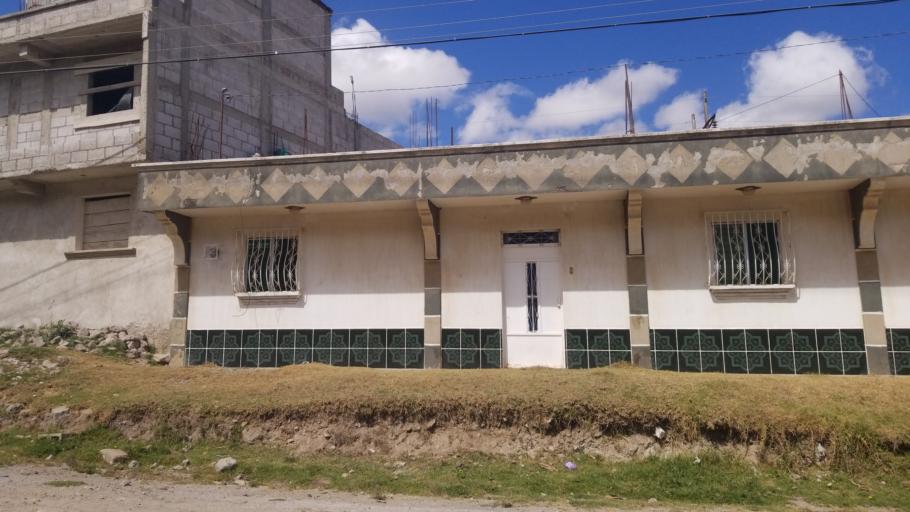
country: GT
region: Quetzaltenango
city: Almolonga
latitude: 14.7951
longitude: -91.5373
